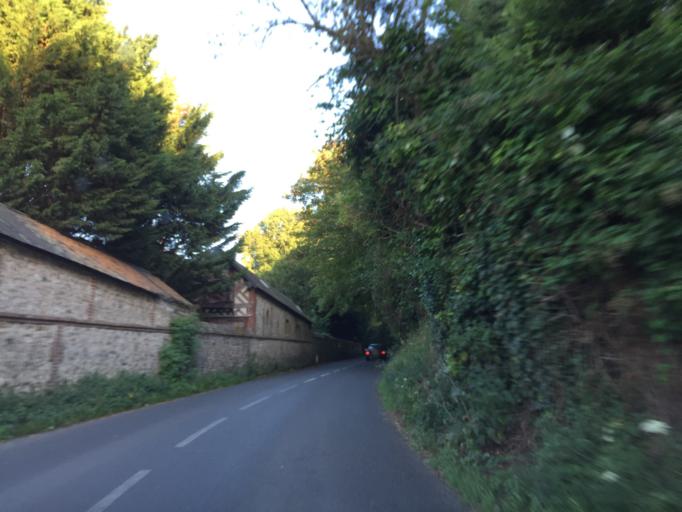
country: FR
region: Lower Normandy
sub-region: Departement du Calvados
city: Equemauville
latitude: 49.4188
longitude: 0.1988
